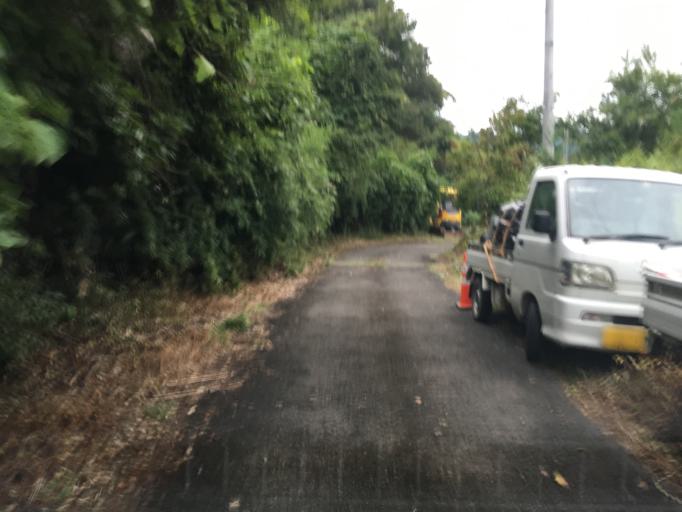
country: JP
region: Fukushima
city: Hobaramachi
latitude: 37.7619
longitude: 140.5369
